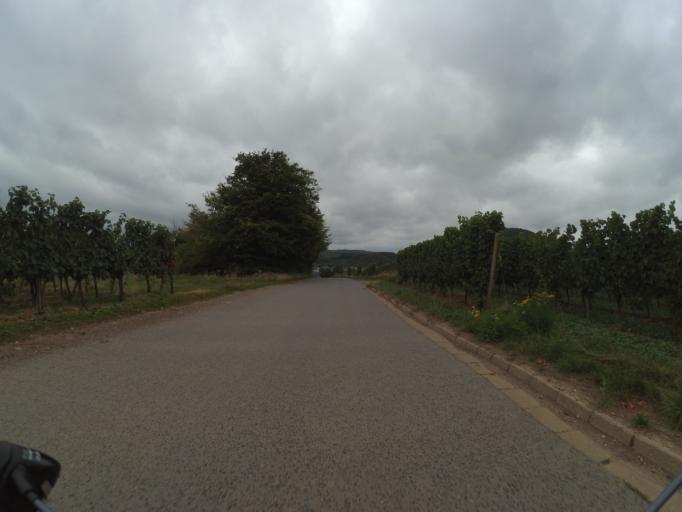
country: DE
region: Rheinland-Pfalz
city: Klusserath
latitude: 49.8322
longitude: 6.8506
